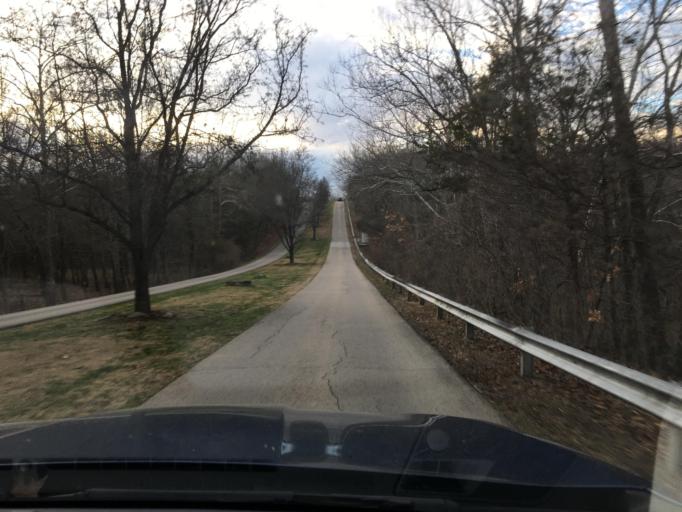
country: US
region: Missouri
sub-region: Jefferson County
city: De Soto
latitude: 38.0913
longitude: -90.5628
